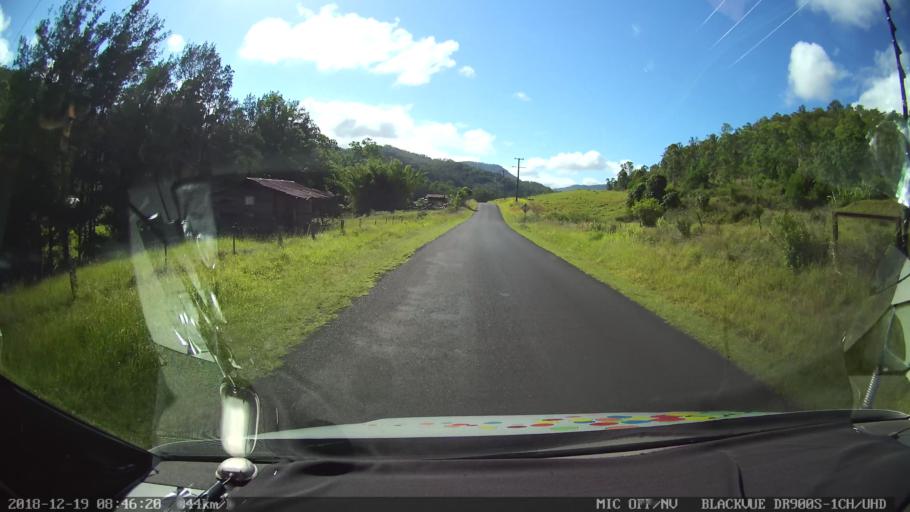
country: AU
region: New South Wales
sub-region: Kyogle
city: Kyogle
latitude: -28.3609
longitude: 152.9681
